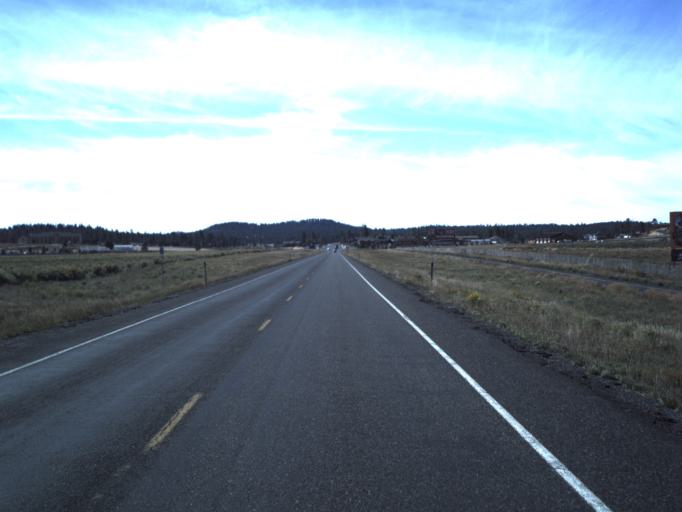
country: US
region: Utah
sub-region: Garfield County
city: Panguitch
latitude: 37.6839
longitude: -112.1539
